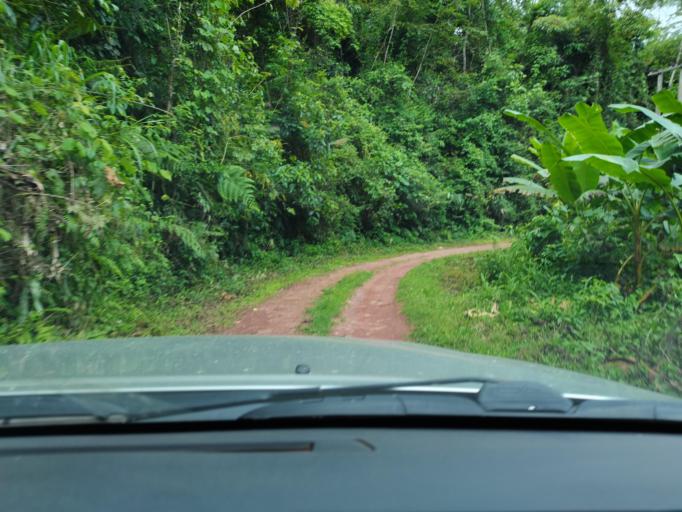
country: LA
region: Loungnamtha
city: Muang Nale
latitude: 20.5154
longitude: 101.0734
